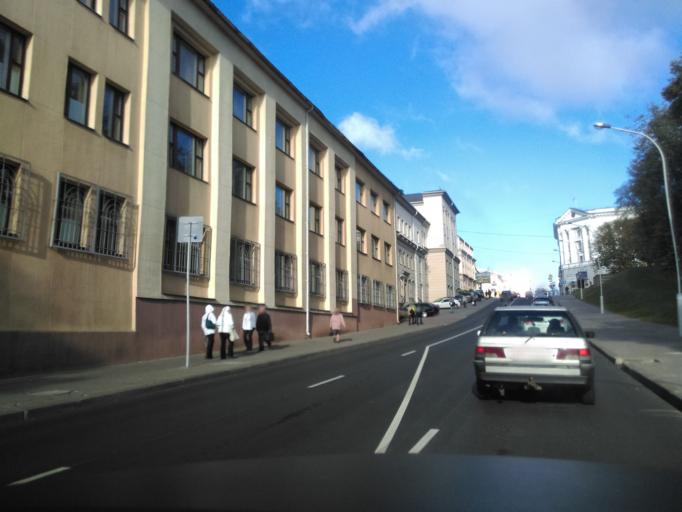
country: BY
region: Minsk
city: Minsk
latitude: 53.8969
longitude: 27.5638
